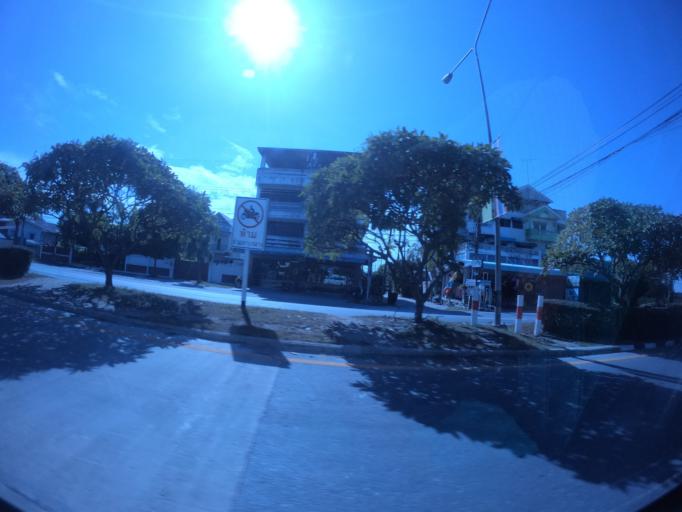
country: TH
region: Nakhon Nayok
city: Ban Na
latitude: 14.2581
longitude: 101.0729
